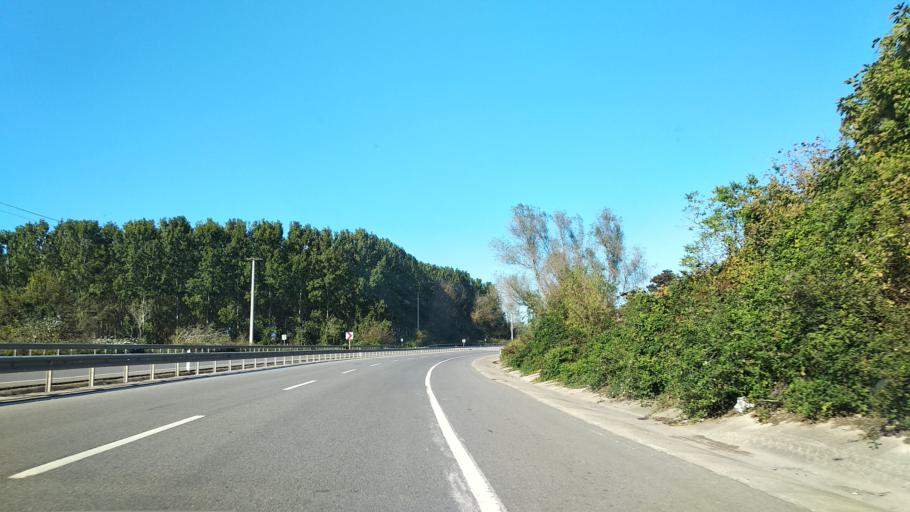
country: TR
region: Sakarya
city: Karasu
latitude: 41.0877
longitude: 30.6471
